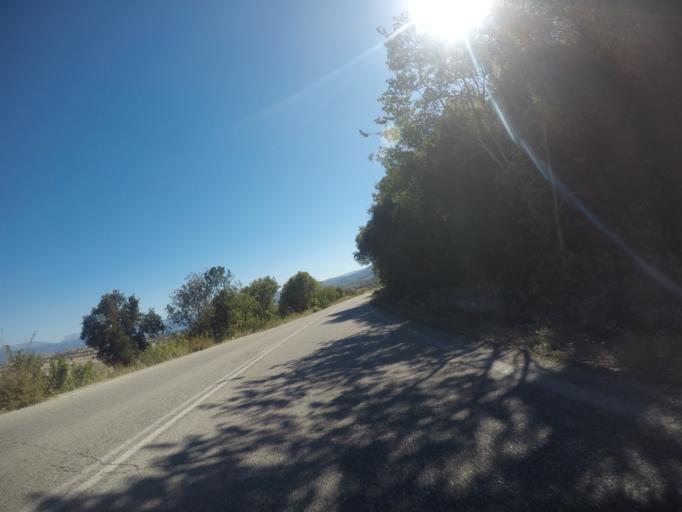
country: GR
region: West Greece
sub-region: Nomos Aitolias kai Akarnanias
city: Monastirakion
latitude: 38.9009
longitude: 20.9844
